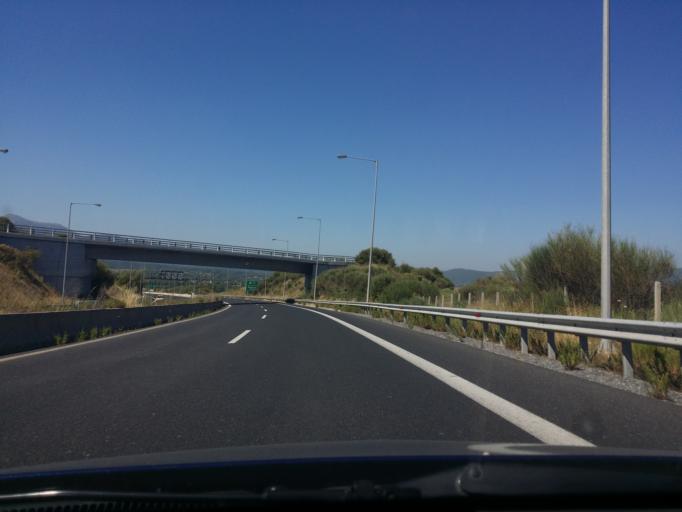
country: GR
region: Peloponnese
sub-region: Nomos Arkadias
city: Megalopoli
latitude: 37.3931
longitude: 22.1744
